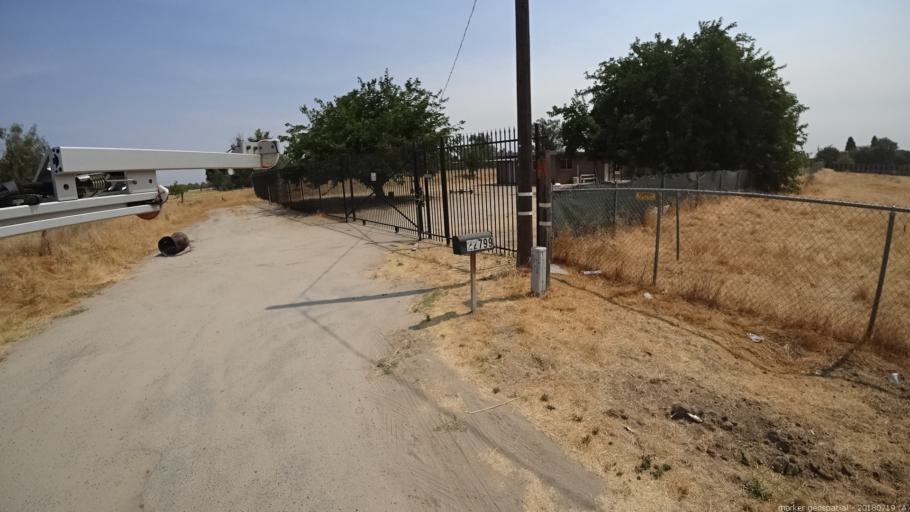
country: US
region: California
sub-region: Madera County
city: Fairmead
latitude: 37.0820
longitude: -120.1985
